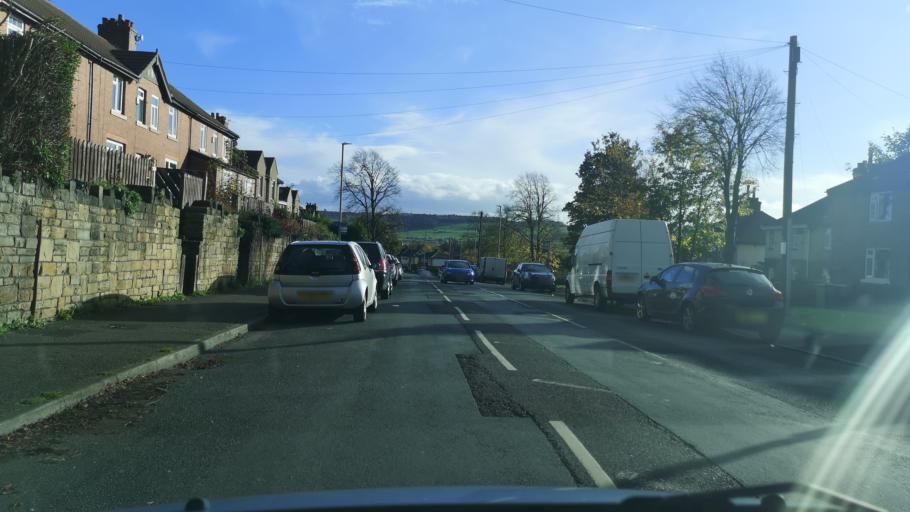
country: GB
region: England
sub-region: Kirklees
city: Dewsbury
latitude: 53.6869
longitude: -1.6553
